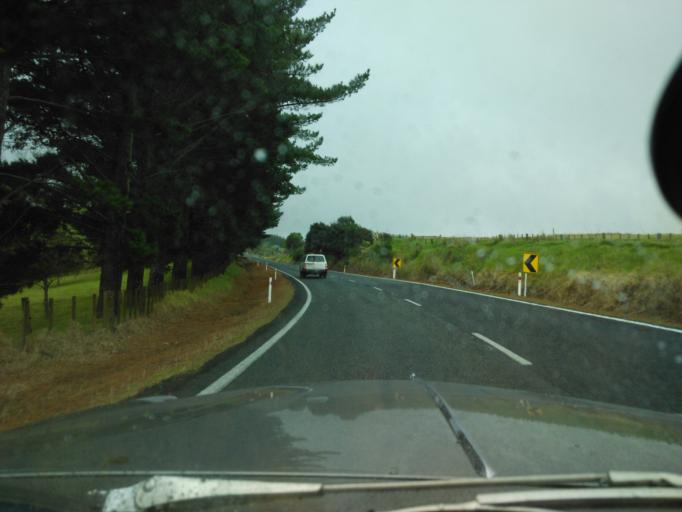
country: NZ
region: Auckland
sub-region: Auckland
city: Parakai
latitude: -36.4682
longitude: 174.4467
